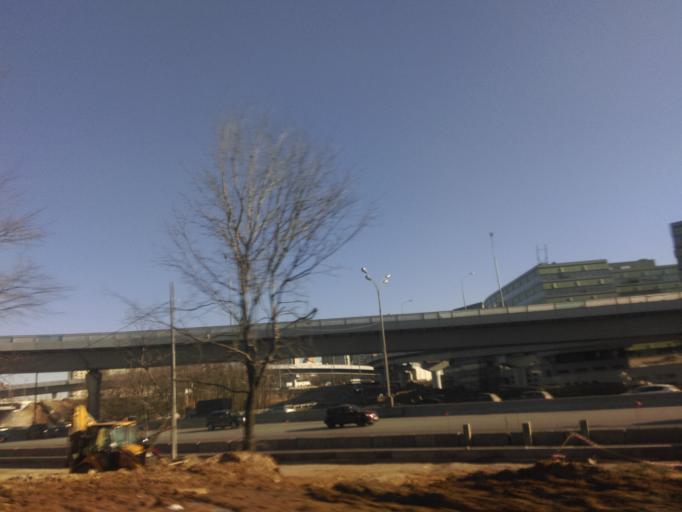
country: RU
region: Moskovskaya
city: Marfino
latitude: 55.7114
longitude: 37.3865
